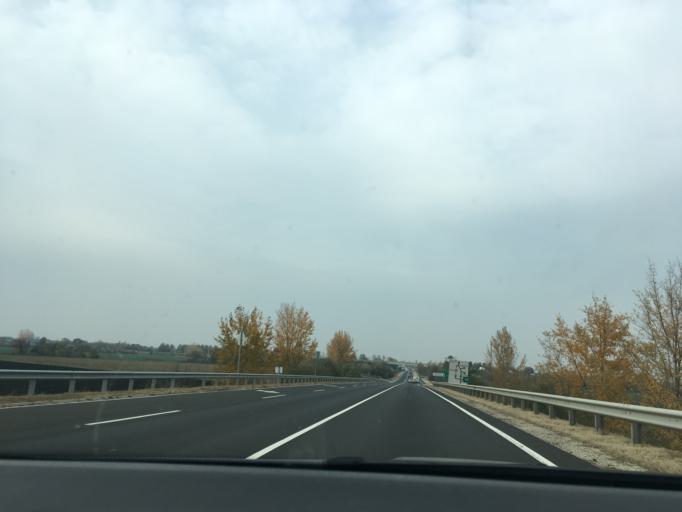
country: HU
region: Jasz-Nagykun-Szolnok
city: Toszeg
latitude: 47.1774
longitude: 20.1012
